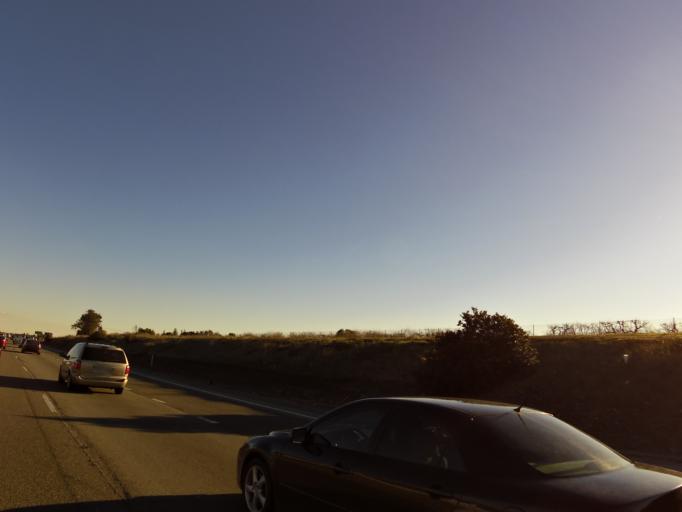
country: US
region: California
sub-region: Santa Clara County
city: Morgan Hill
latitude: 37.1608
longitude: -121.6615
